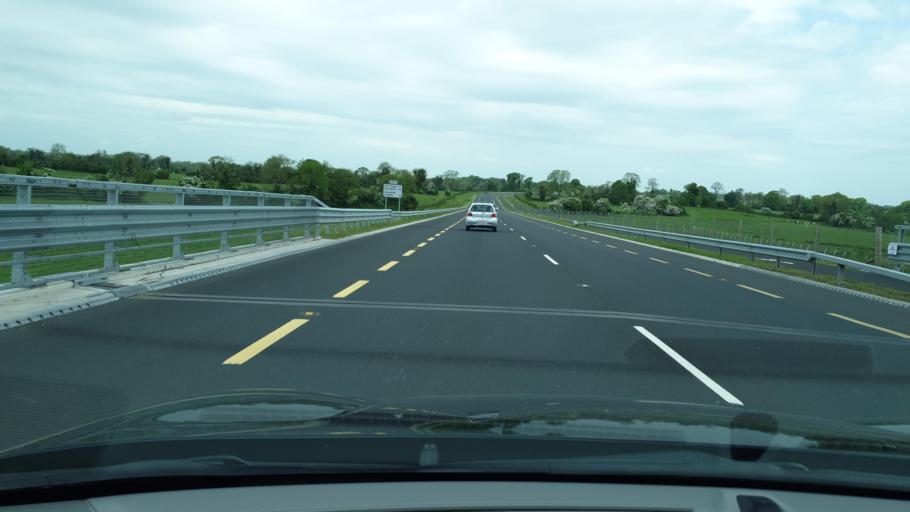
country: IE
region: Leinster
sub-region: Kildare
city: Sallins
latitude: 53.2508
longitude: -6.6806
